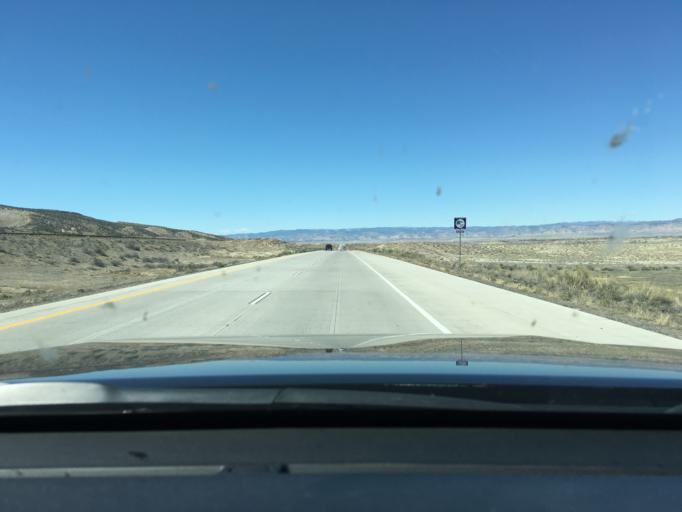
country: US
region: Colorado
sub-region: Mesa County
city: Loma
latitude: 39.1934
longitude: -108.8415
